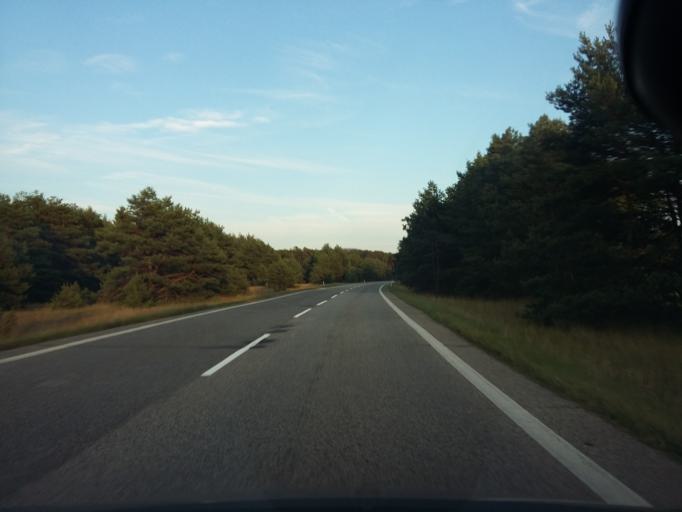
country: SK
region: Bratislavsky
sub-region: Okres Malacky
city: Malacky
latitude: 48.4070
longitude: 17.0767
